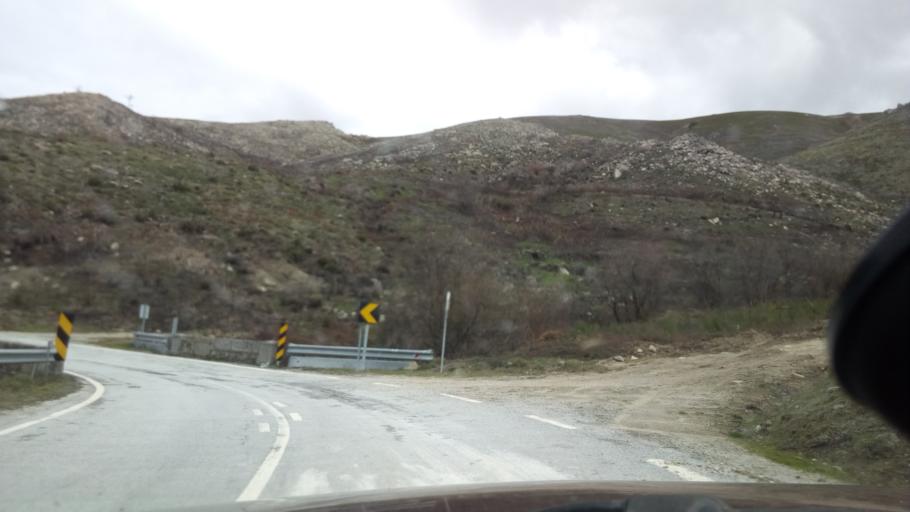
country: PT
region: Guarda
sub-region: Manteigas
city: Manteigas
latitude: 40.4499
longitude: -7.5863
